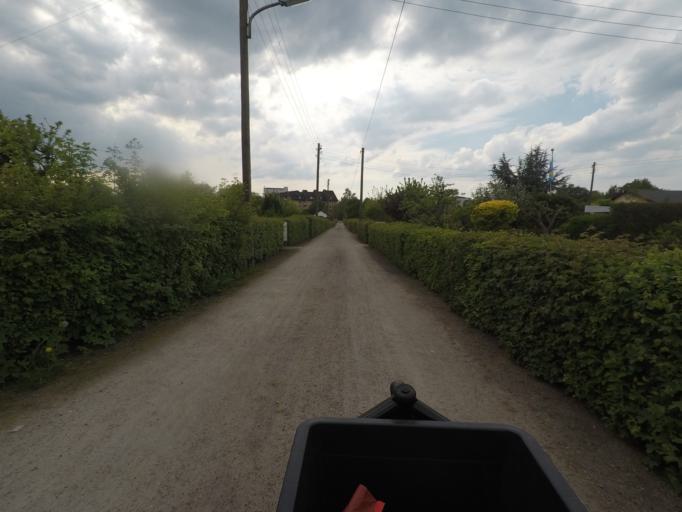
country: DE
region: Hamburg
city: Steilshoop
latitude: 53.6027
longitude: 10.0889
